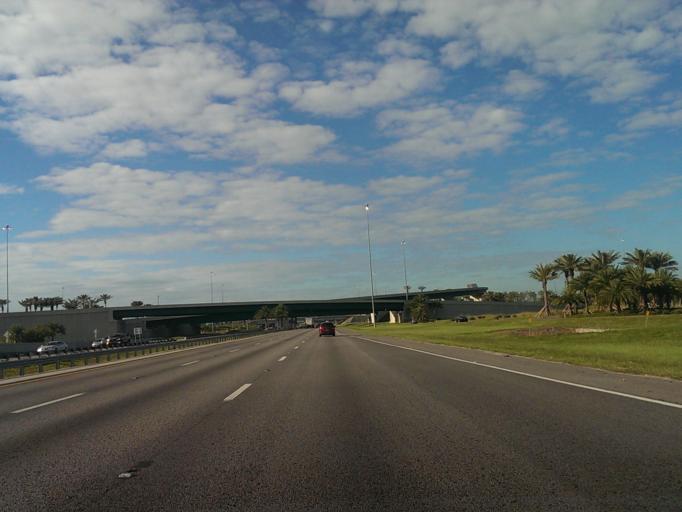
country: US
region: Florida
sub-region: Osceola County
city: Celebration
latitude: 28.3355
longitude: -81.5430
